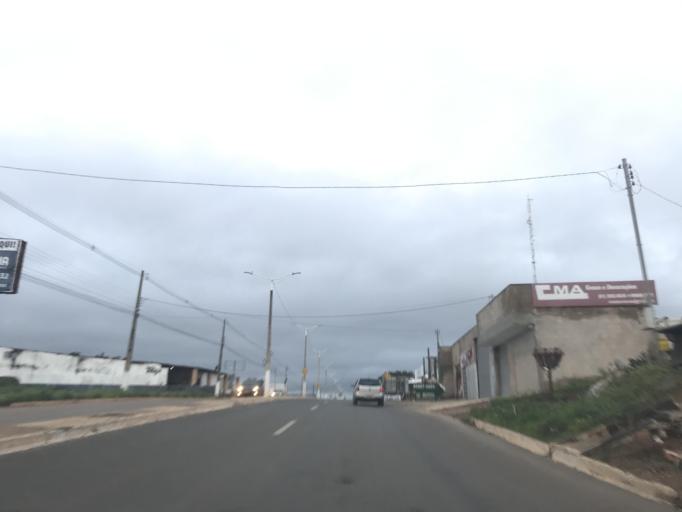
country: BR
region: Goias
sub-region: Luziania
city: Luziania
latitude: -16.2164
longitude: -47.9318
